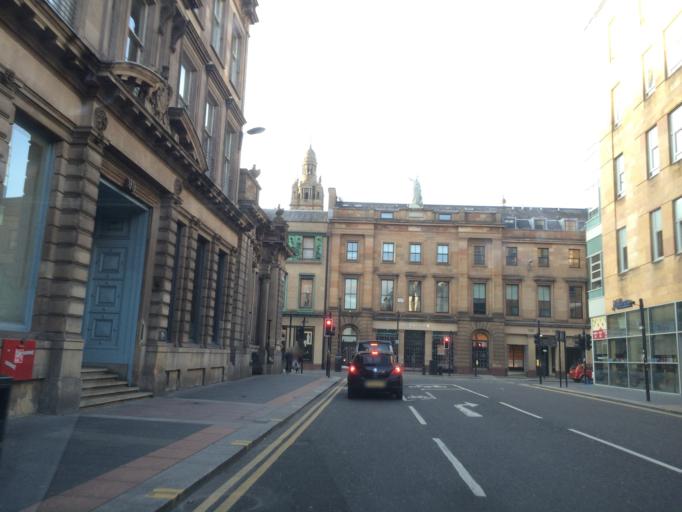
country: GB
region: Scotland
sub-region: Glasgow City
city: Glasgow
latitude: 55.8594
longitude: -4.2487
